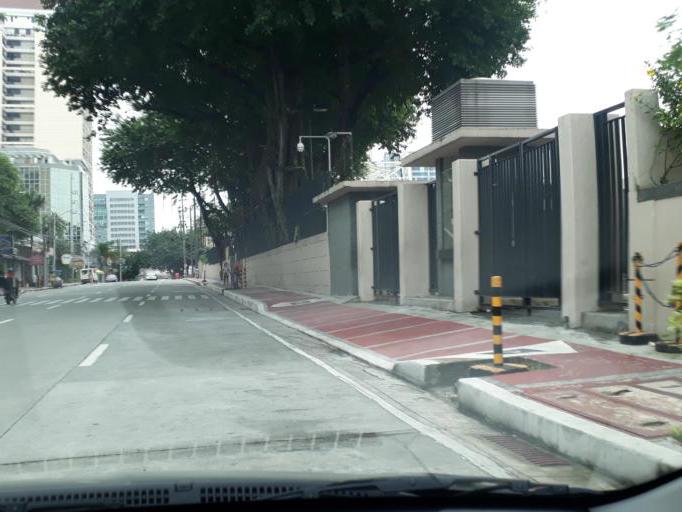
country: PH
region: Metro Manila
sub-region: Quezon City
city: Quezon City
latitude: 14.6401
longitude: 121.0356
